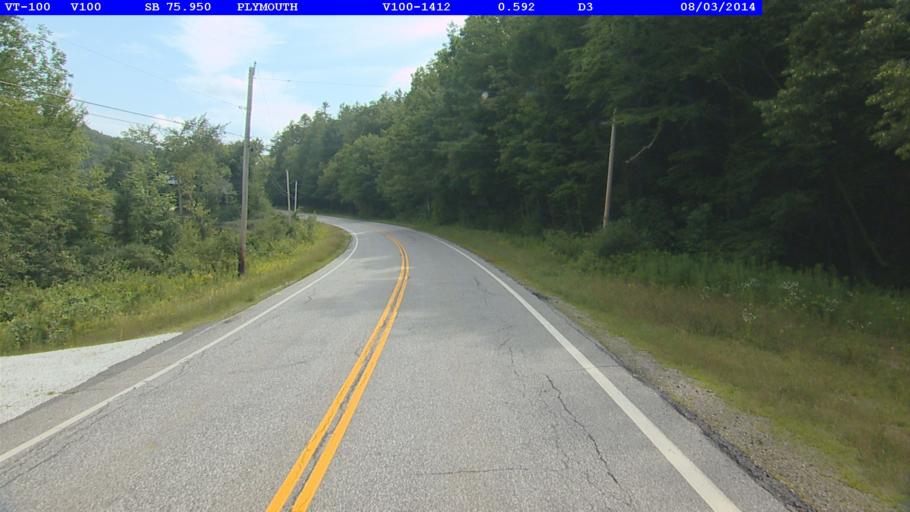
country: US
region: Vermont
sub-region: Windsor County
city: Chester
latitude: 43.4711
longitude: -72.7033
